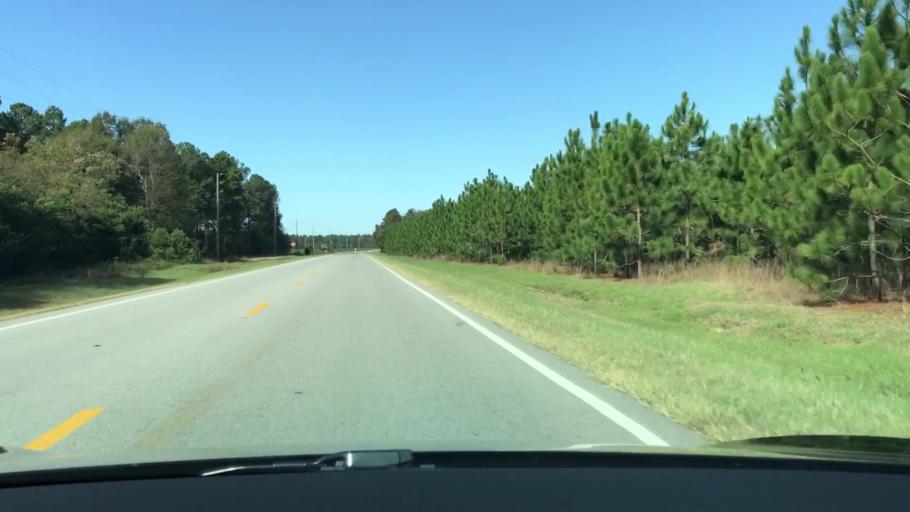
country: US
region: Georgia
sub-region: Glascock County
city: Gibson
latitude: 33.3092
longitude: -82.5347
